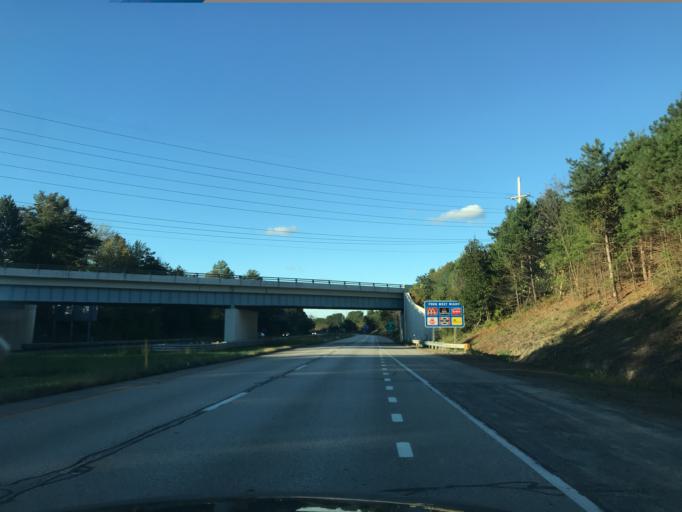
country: US
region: Ohio
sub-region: Ashtabula County
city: Edgewood
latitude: 41.8656
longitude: -80.7625
